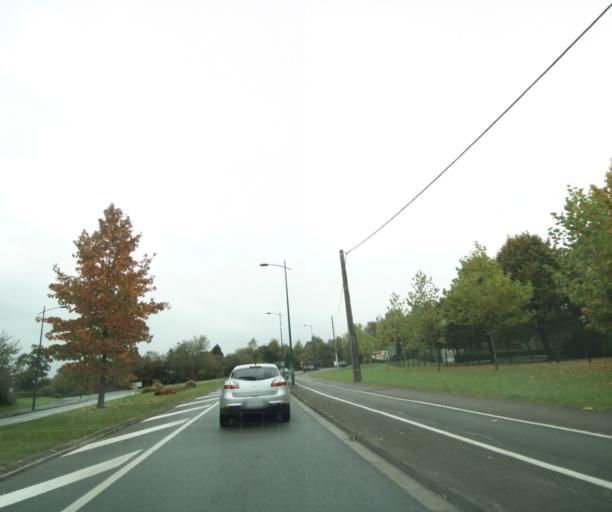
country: FR
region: Nord-Pas-de-Calais
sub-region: Departement du Nord
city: Roncq
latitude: 50.7643
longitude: 3.1213
